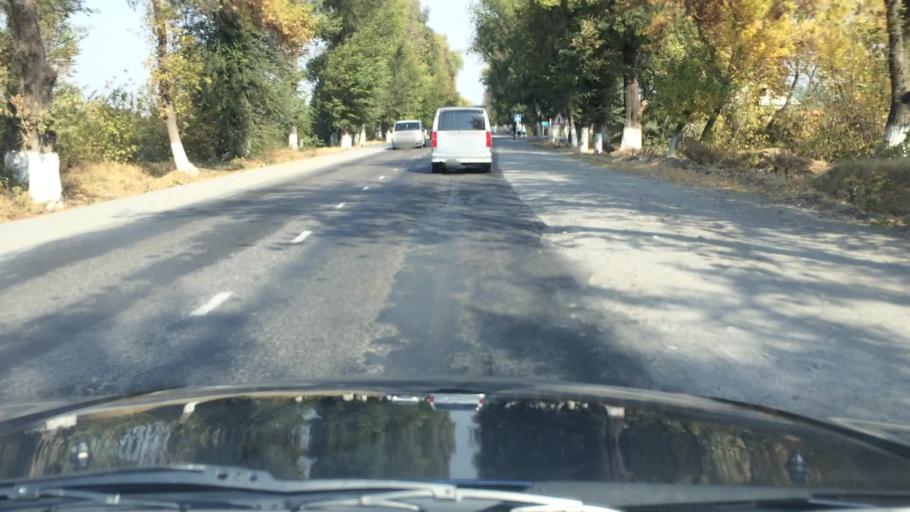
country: KG
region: Chuy
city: Lebedinovka
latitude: 42.9201
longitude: 74.6894
